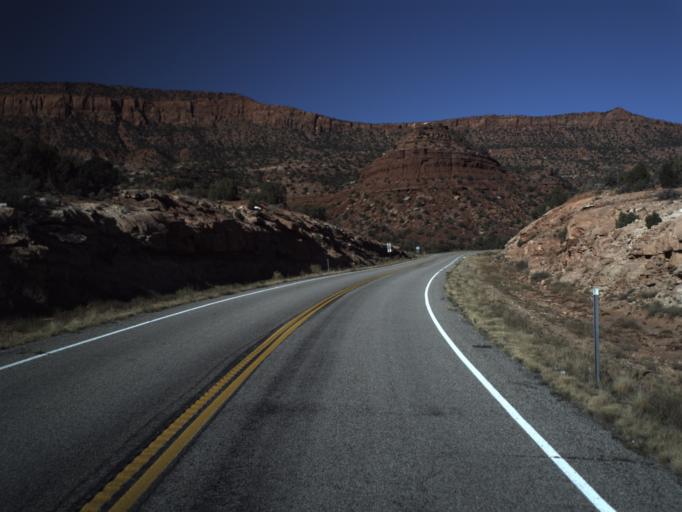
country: US
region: Utah
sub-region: San Juan County
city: Blanding
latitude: 37.6356
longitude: -110.1528
